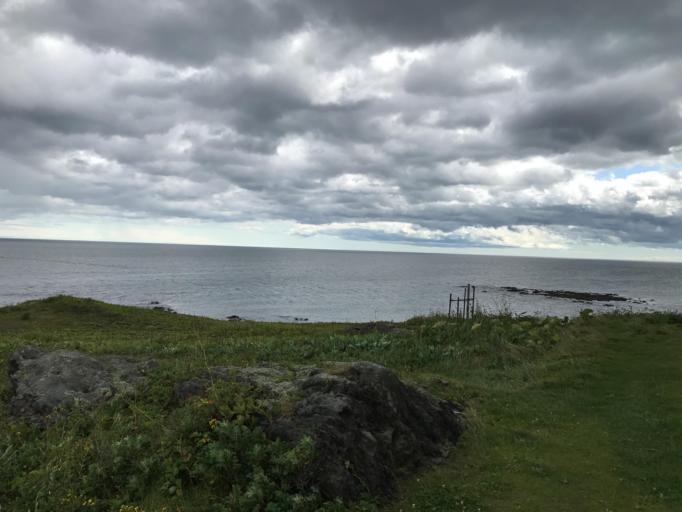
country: JP
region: Hokkaido
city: Mombetsu
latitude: 44.5309
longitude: 143.0612
